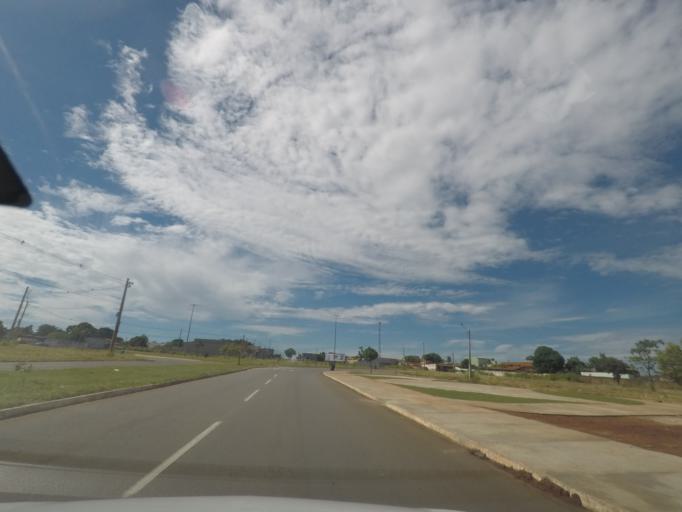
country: BR
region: Goias
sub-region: Aparecida De Goiania
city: Aparecida de Goiania
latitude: -16.8031
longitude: -49.2826
